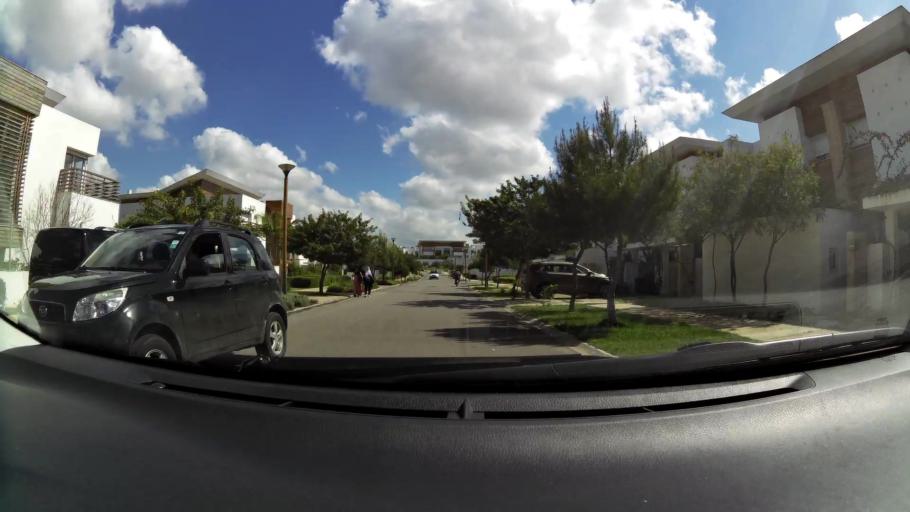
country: MA
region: Grand Casablanca
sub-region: Nouaceur
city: Bouskoura
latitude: 33.4889
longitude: -7.5997
